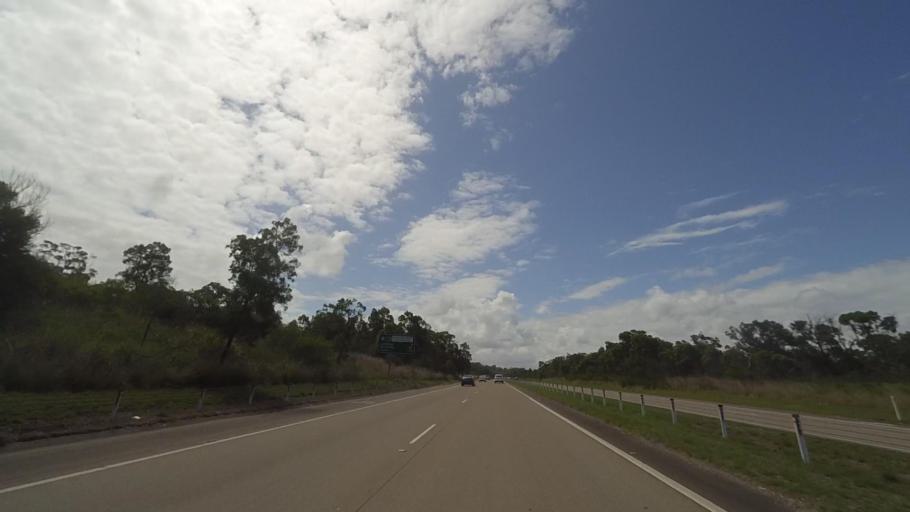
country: AU
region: New South Wales
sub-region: Lake Macquarie Shire
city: Windale
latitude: -32.9888
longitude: 151.6868
